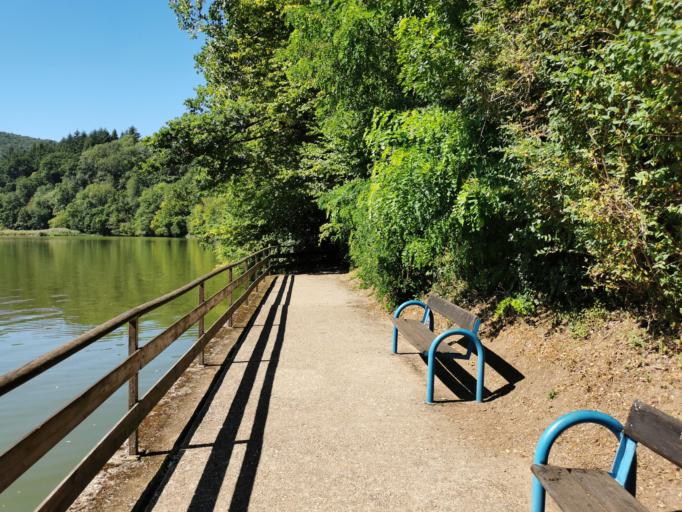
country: DE
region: Rheinland-Pfalz
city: Echtershausen
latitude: 50.0191
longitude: 6.4321
